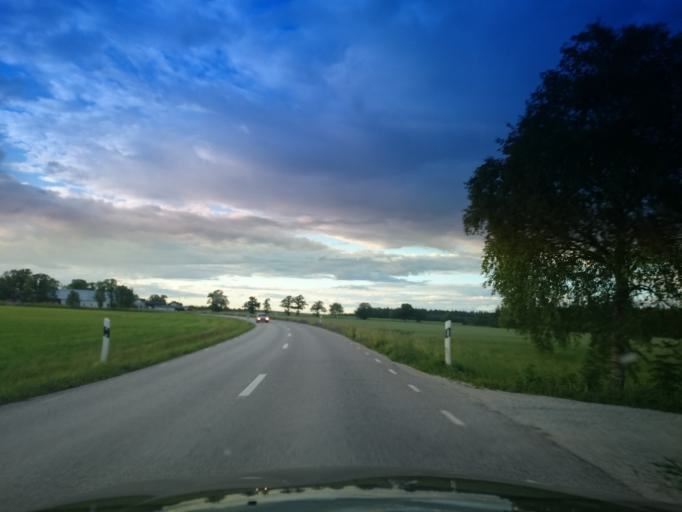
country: SE
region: Gotland
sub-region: Gotland
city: Vibble
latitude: 57.5002
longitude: 18.3723
